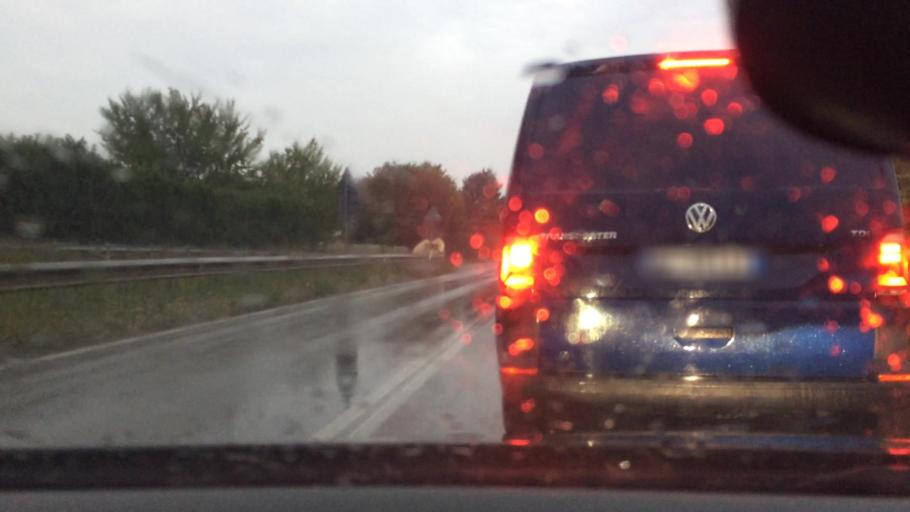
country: IT
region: Lombardy
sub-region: Citta metropolitana di Milano
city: Vanzago
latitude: 45.5311
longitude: 8.9883
